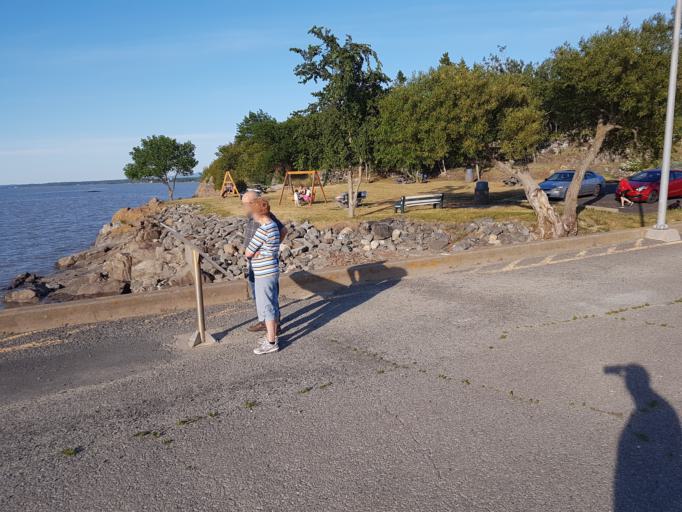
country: CA
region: Quebec
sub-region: Chaudiere-Appalaches
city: Montmagny
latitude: 47.1341
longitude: -70.3704
